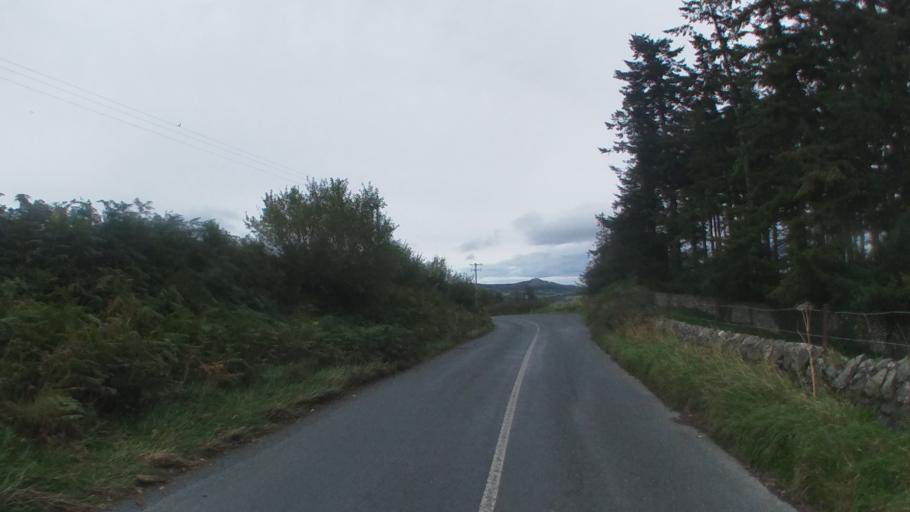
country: IE
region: Leinster
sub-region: Wicklow
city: Enniskerry
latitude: 53.1950
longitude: -6.1983
